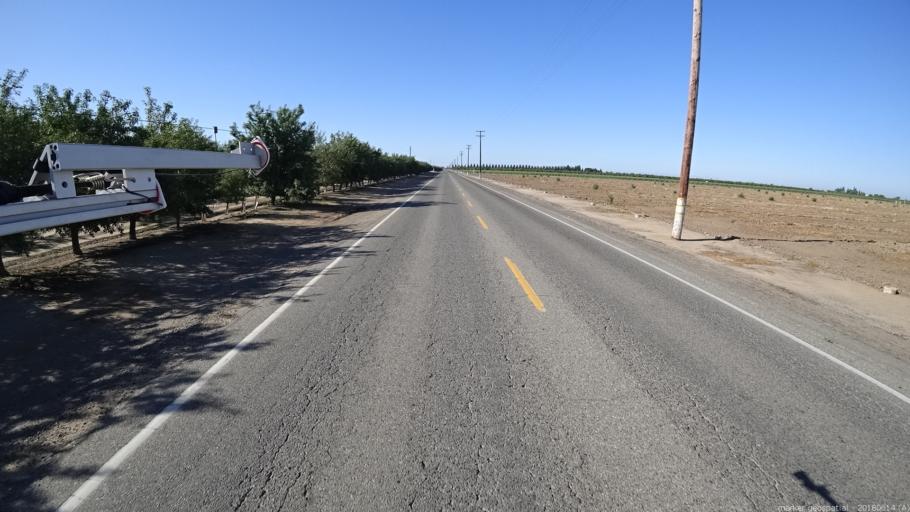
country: US
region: California
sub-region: Madera County
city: Madera
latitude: 36.9766
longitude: -120.1285
